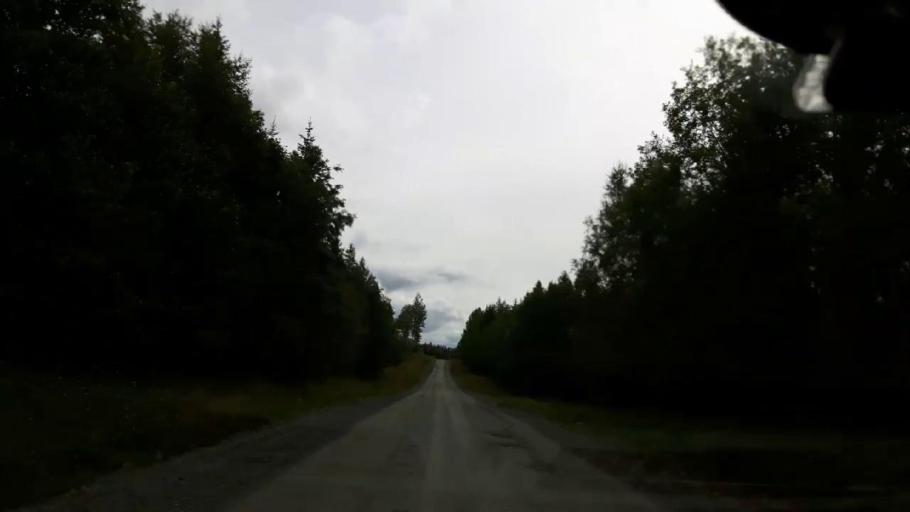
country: SE
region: Jaemtland
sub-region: Krokoms Kommun
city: Valla
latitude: 63.6545
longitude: 13.9797
